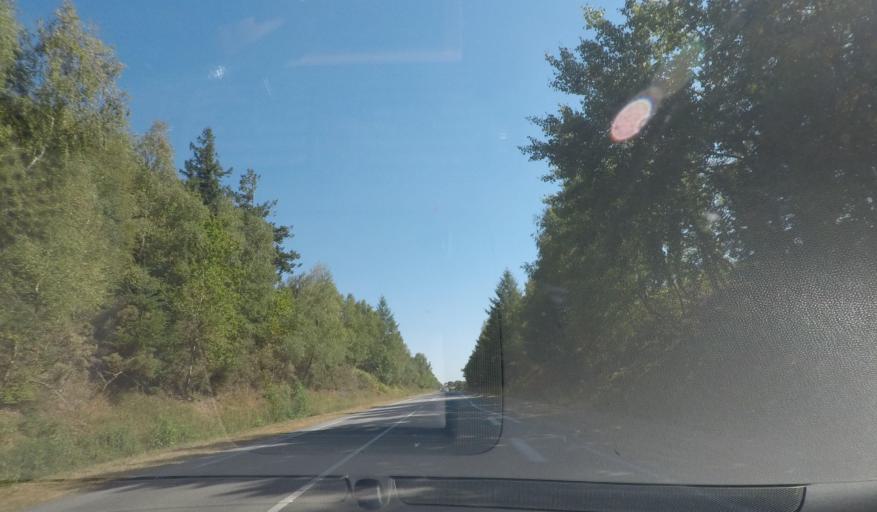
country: FR
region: Brittany
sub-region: Departement du Morbihan
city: Questembert
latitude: 47.6459
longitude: -2.4275
